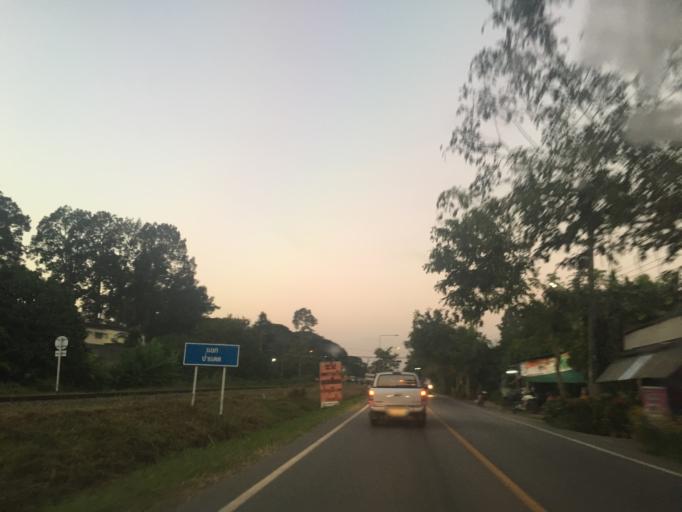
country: TH
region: Chiang Mai
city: Saraphi
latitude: 18.6921
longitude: 99.0454
